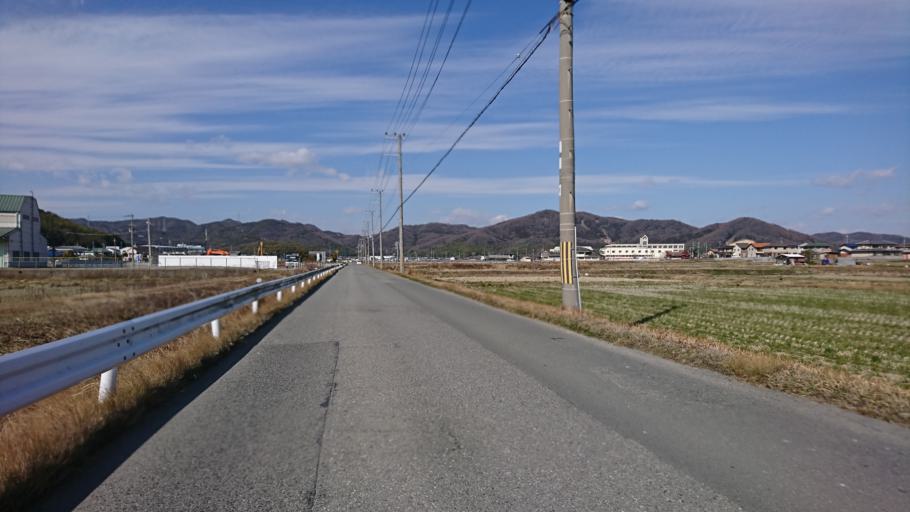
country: JP
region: Hyogo
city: Kakogawacho-honmachi
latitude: 34.8114
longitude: 134.8079
